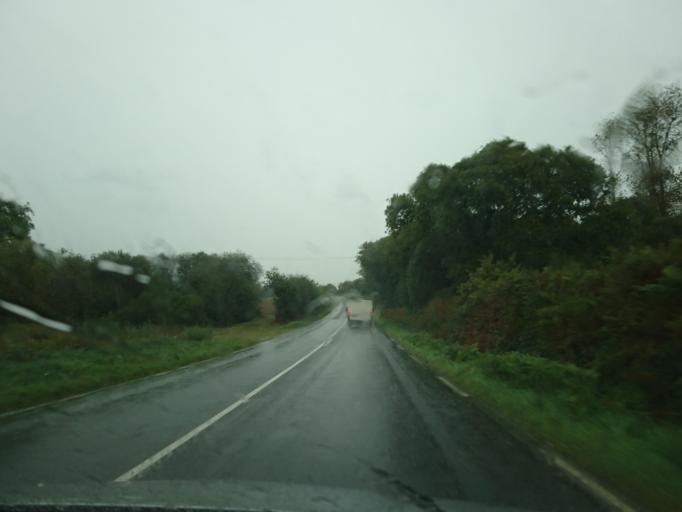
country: FR
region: Brittany
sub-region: Departement du Finistere
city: Gouesnou
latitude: 48.4680
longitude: -4.4460
